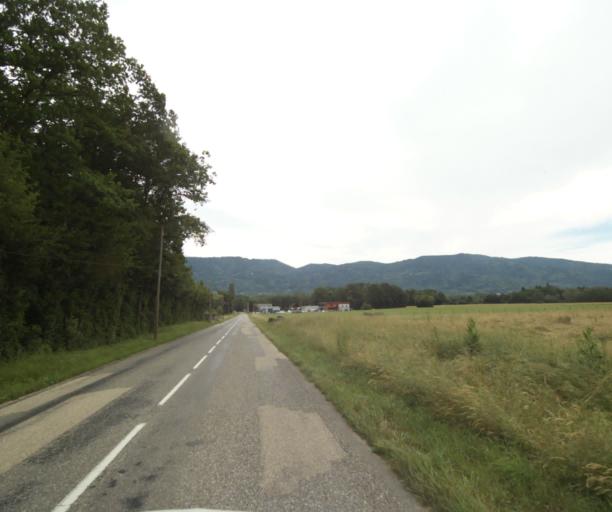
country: FR
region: Rhone-Alpes
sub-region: Departement de la Haute-Savoie
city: Perrignier
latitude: 46.3032
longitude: 6.4135
